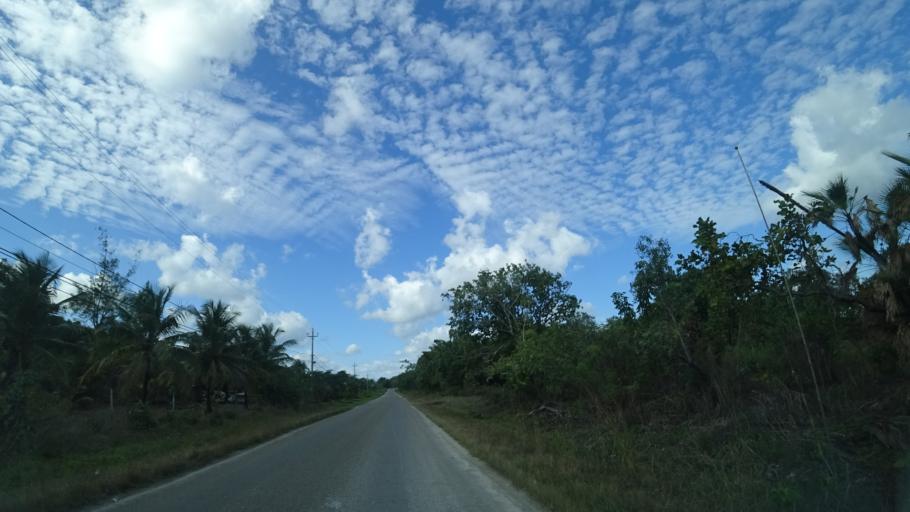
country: BZ
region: Belize
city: Belize City
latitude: 17.5625
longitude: -88.4055
